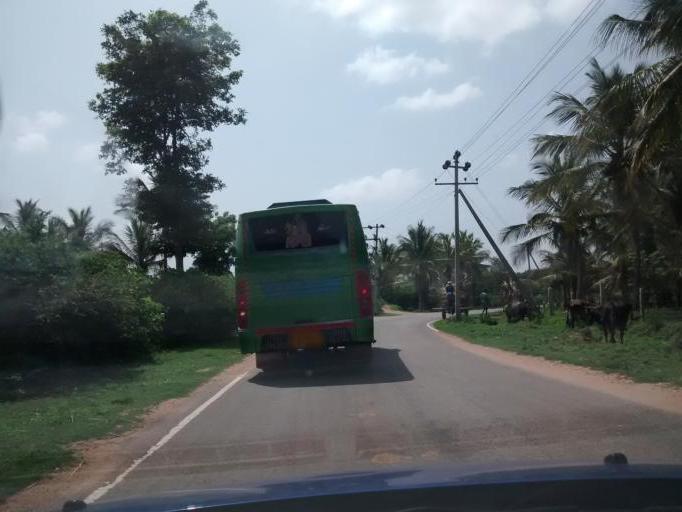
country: IN
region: Karnataka
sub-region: Hassan
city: Konanur
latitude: 12.6542
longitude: 76.1844
